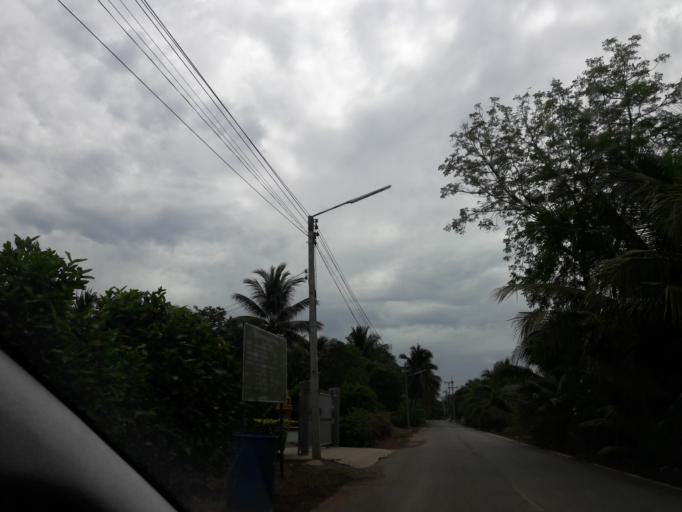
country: TH
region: Ratchaburi
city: Damnoen Saduak
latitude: 13.5326
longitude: 99.9491
